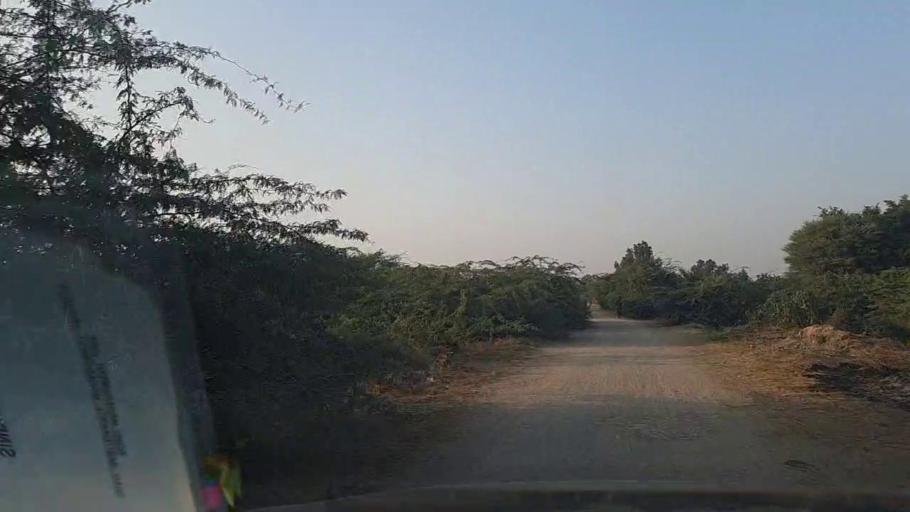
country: PK
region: Sindh
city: Keti Bandar
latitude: 24.3116
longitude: 67.6007
